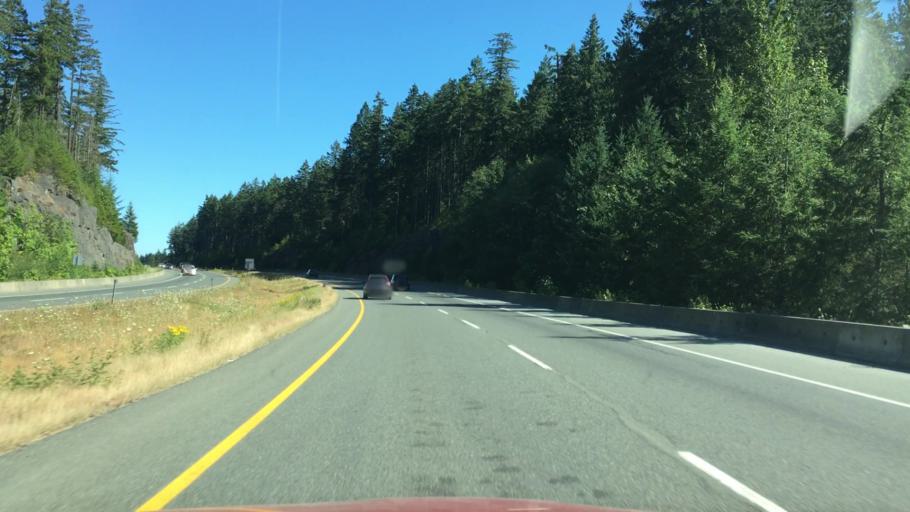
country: CA
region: British Columbia
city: Nanaimo
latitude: 49.1453
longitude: -123.9716
